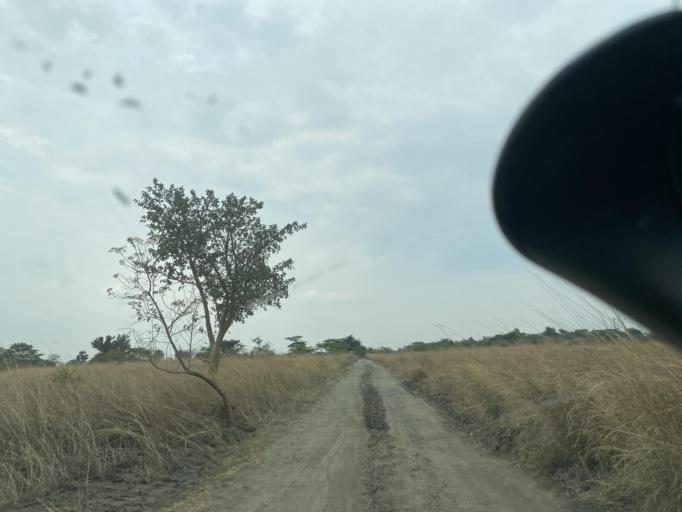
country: ZM
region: Lusaka
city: Lusaka
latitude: -15.2464
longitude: 28.3324
